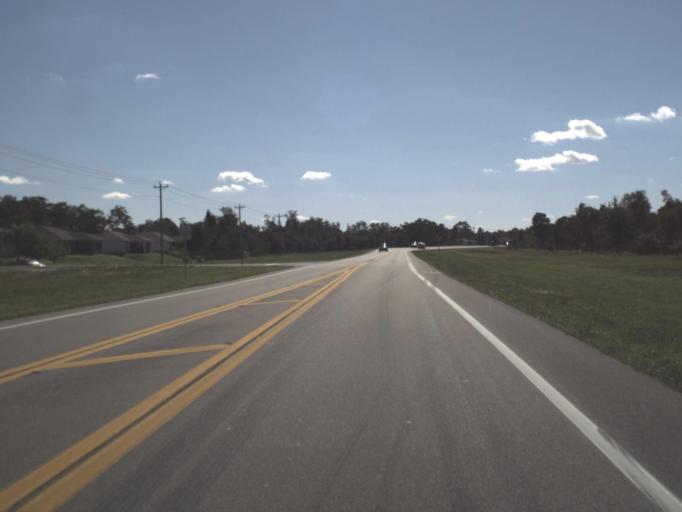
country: US
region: Florida
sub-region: Lee County
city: Lehigh Acres
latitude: 26.5474
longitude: -81.6400
